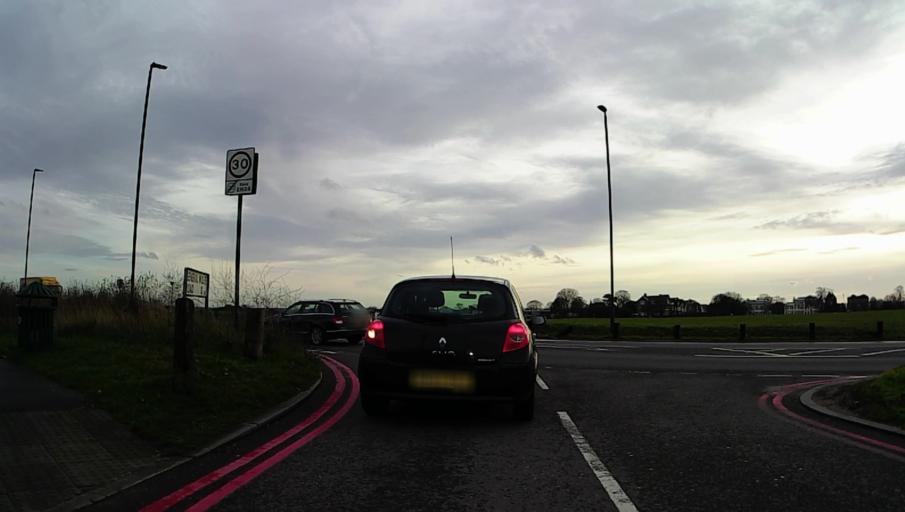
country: GB
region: England
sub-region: Greater London
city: Blackheath
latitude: 51.4721
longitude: -0.0024
